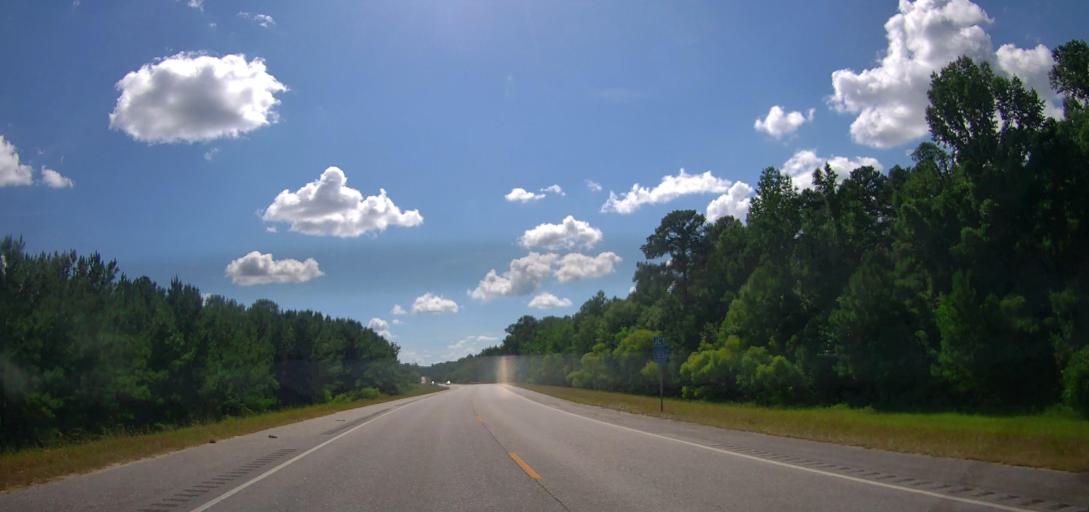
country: US
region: Alabama
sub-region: Macon County
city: Tuskegee
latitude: 32.4437
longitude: -85.6512
